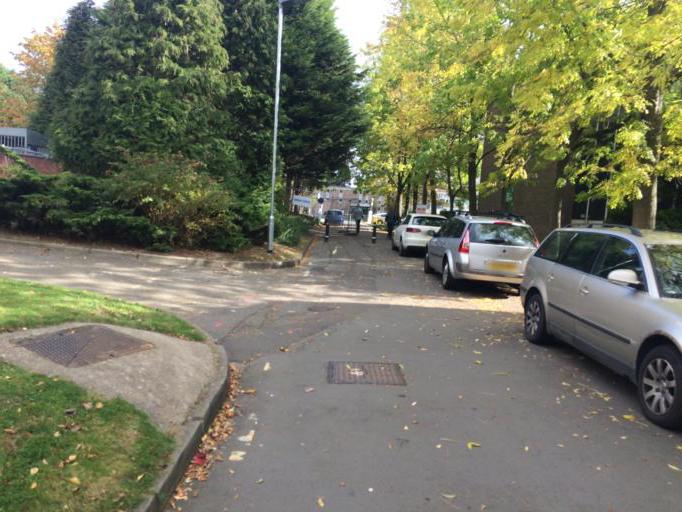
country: GB
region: Scotland
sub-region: Edinburgh
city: Edinburgh
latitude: 55.9220
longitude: -3.1765
